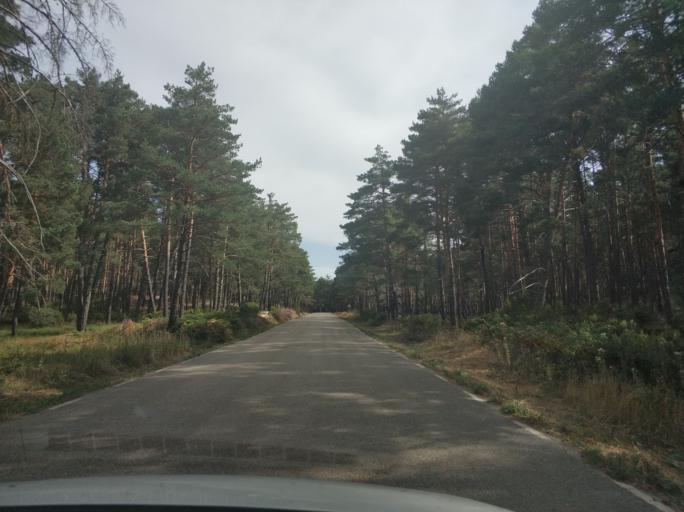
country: ES
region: Castille and Leon
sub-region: Provincia de Soria
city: Navaleno
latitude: 41.8448
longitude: -2.9924
